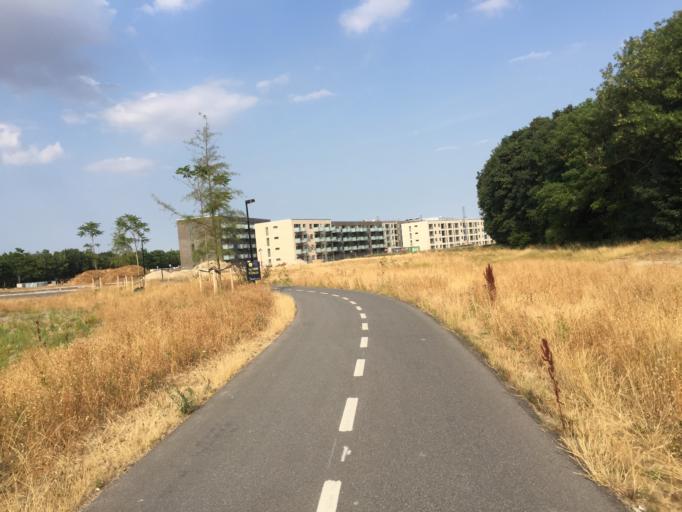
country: DK
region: South Denmark
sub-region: Odense Kommune
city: Neder Holluf
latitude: 55.3734
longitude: 10.4221
